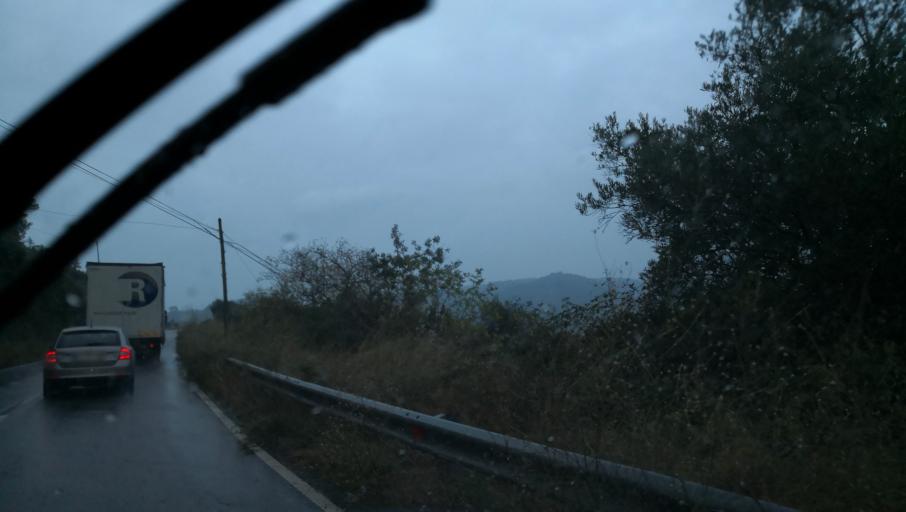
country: PT
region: Vila Real
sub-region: Santa Marta de Penaguiao
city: Santa Marta de Penaguiao
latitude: 41.2260
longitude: -7.7270
